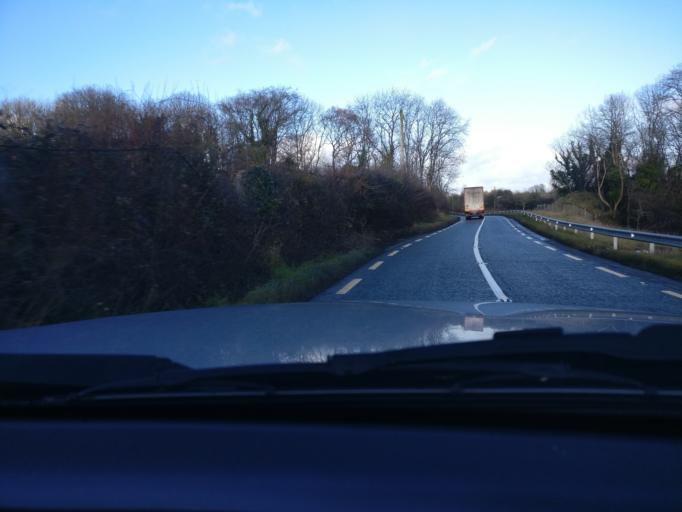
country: IE
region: Leinster
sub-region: An Mhi
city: Athboy
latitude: 53.6486
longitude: -7.0305
